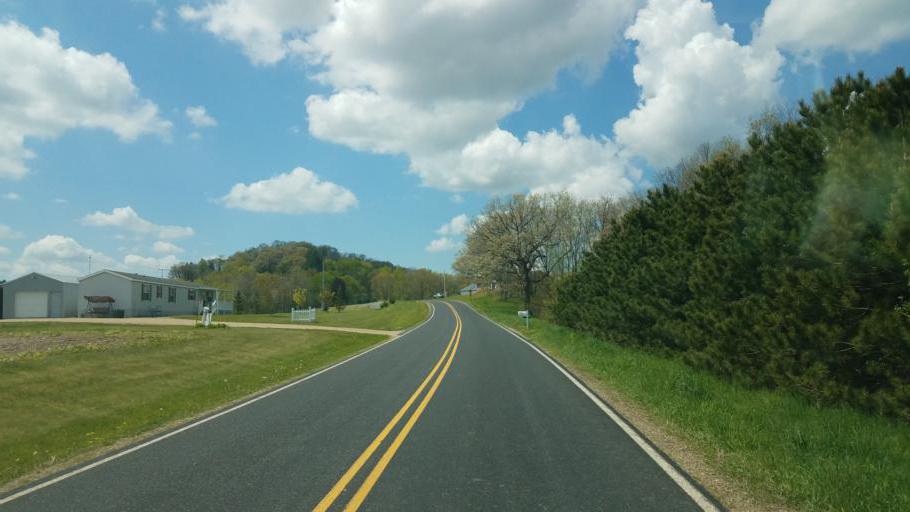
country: US
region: Wisconsin
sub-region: Vernon County
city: Hillsboro
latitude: 43.6823
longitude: -90.3457
